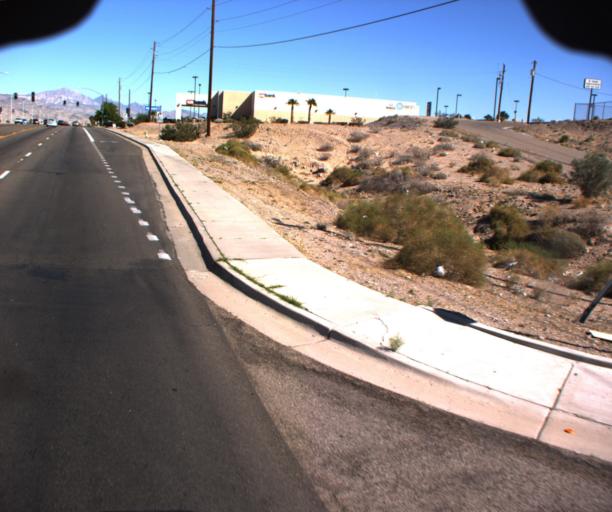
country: US
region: Arizona
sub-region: Mohave County
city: Bullhead City
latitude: 35.0795
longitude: -114.5951
